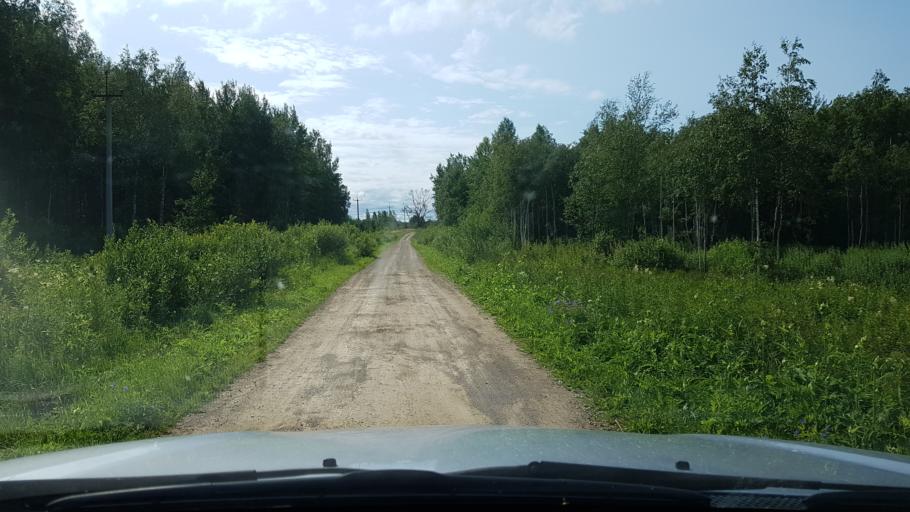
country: EE
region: Ida-Virumaa
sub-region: Narva-Joesuu linn
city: Narva-Joesuu
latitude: 59.3888
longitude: 27.9734
